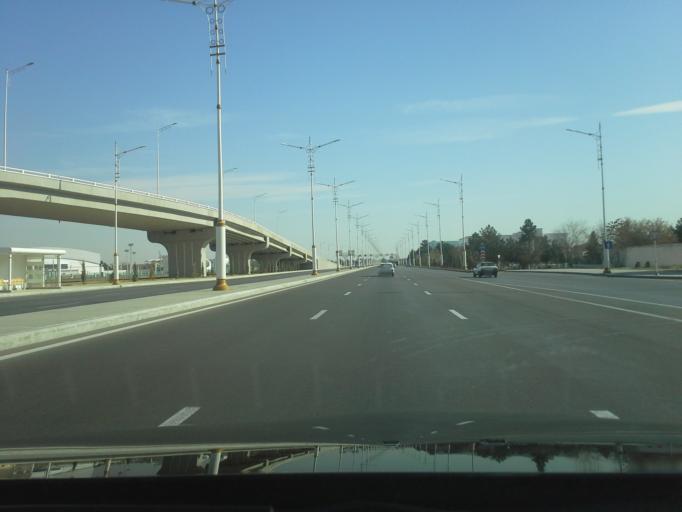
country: TM
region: Ahal
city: Ashgabat
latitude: 37.9255
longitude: 58.4327
